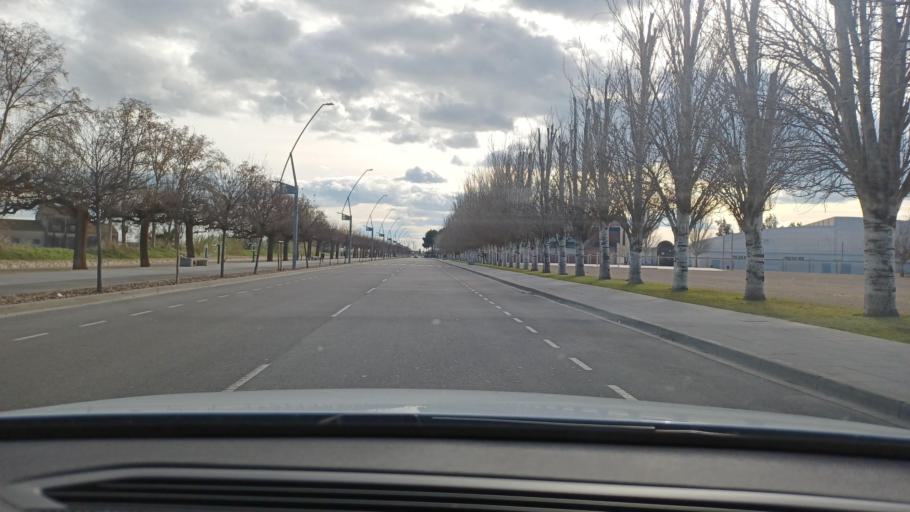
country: ES
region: Catalonia
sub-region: Provincia de Tarragona
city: Amposta
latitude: 40.7080
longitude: 0.5849
